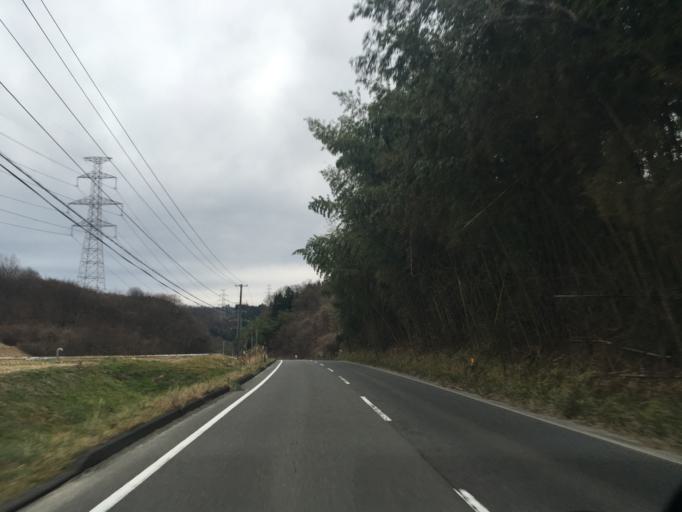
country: JP
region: Fukushima
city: Miharu
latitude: 37.3860
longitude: 140.4477
